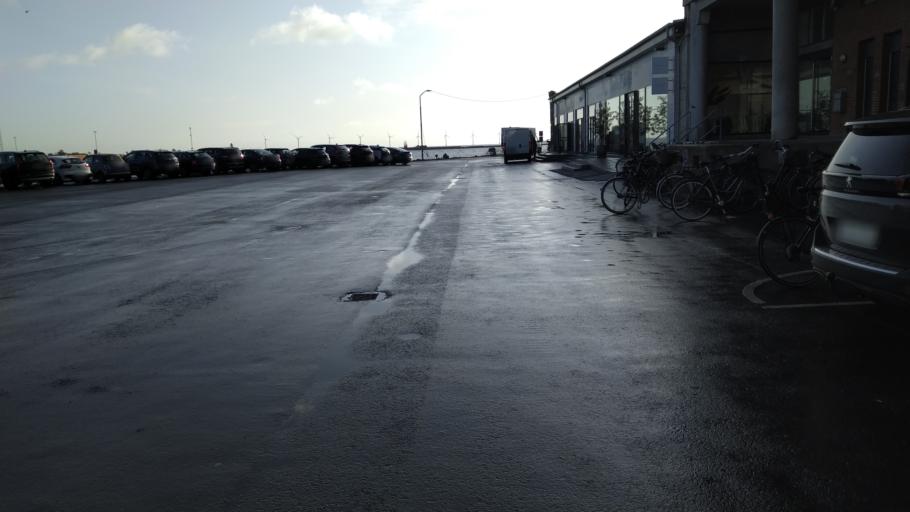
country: DK
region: Capital Region
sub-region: Kobenhavn
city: Christianshavn
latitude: 55.7092
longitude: 12.6031
